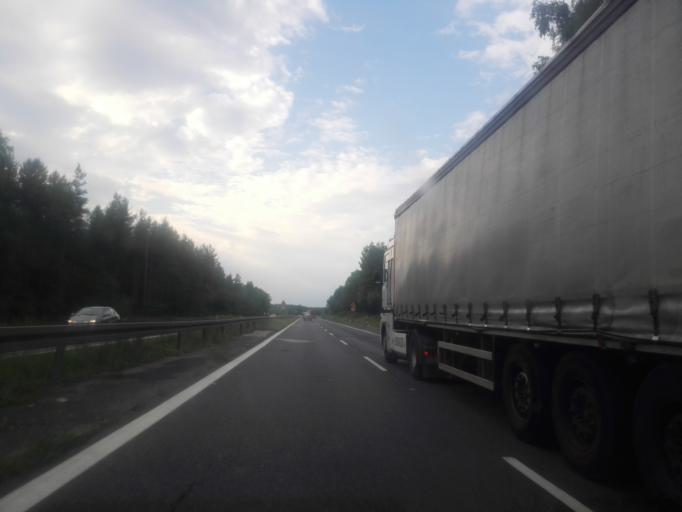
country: PL
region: Silesian Voivodeship
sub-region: Powiat bedzinski
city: Siewierz
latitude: 50.5298
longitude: 19.1912
